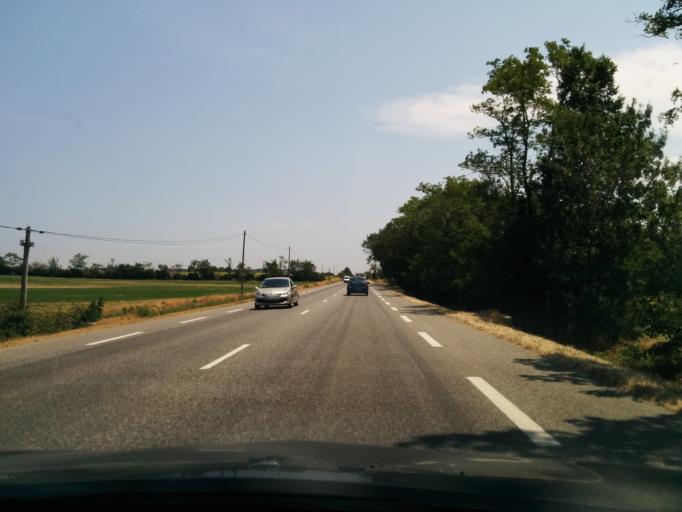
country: FR
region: Midi-Pyrenees
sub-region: Departement de la Haute-Garonne
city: Avignonet-Lauragais
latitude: 43.3742
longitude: 1.7618
